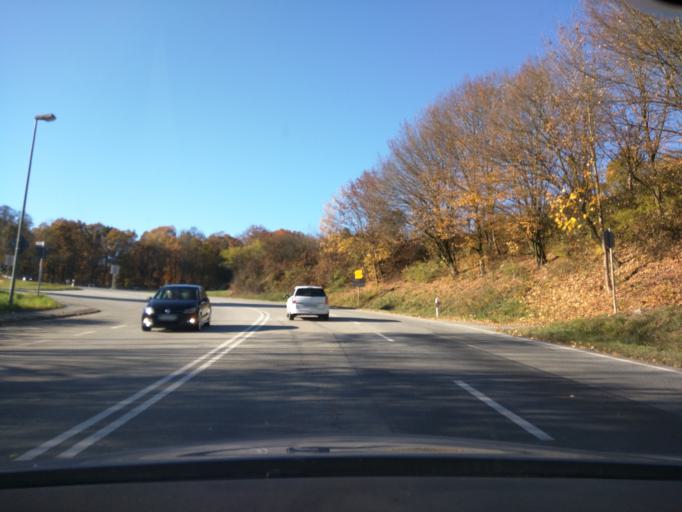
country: DE
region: Bavaria
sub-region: Lower Bavaria
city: Salzweg
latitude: 48.5848
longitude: 13.4748
